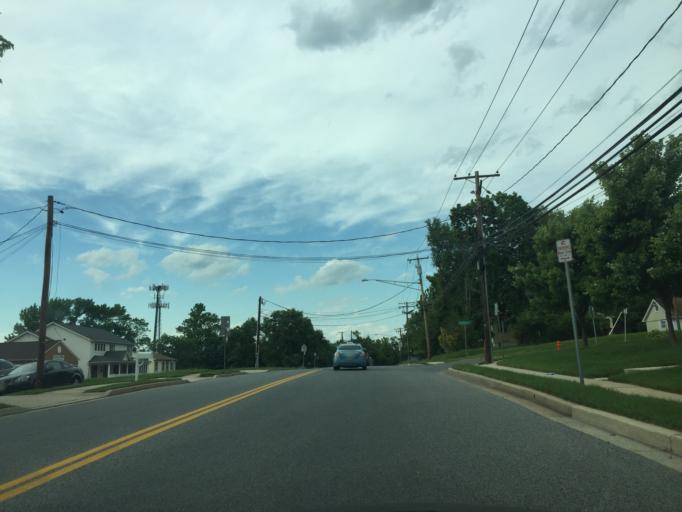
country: US
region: Maryland
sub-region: Baltimore County
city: Rossville
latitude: 39.3255
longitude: -76.4712
